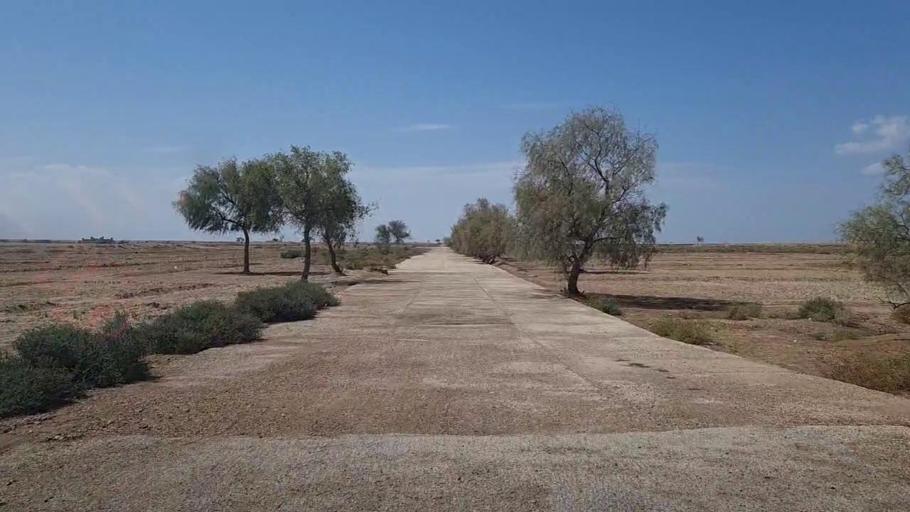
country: PK
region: Sindh
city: Sehwan
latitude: 26.3539
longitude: 67.6717
